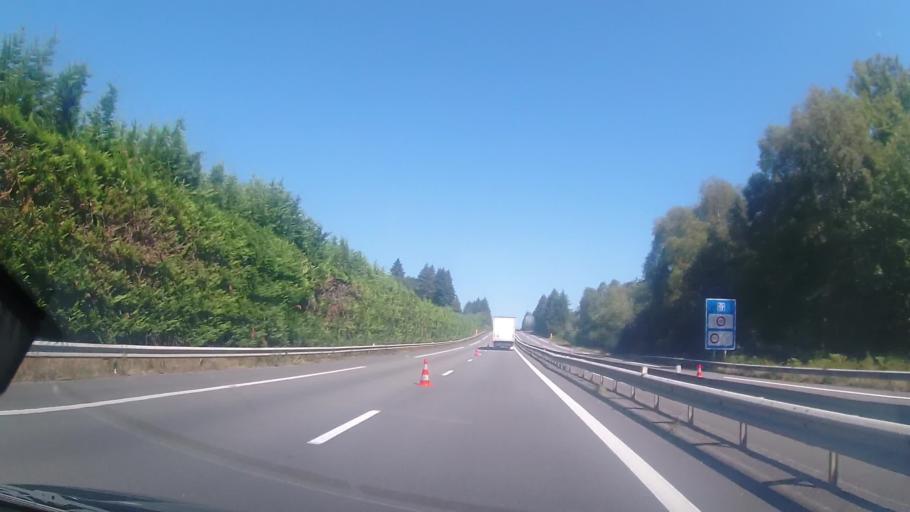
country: FR
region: Limousin
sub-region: Departement de la Haute-Vienne
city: Razes
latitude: 46.0206
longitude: 1.3417
